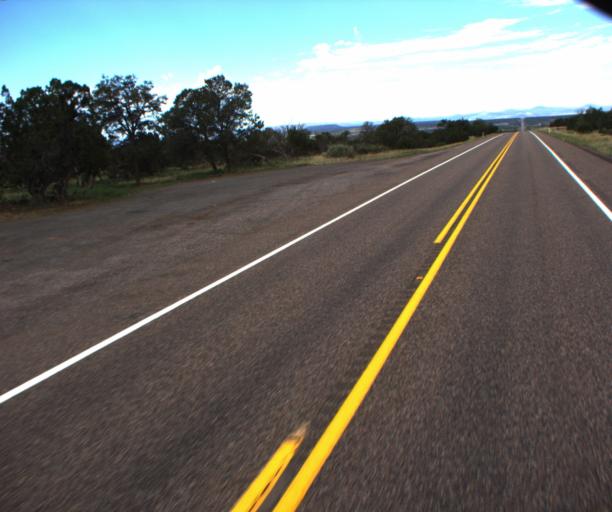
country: US
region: Arizona
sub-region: Apache County
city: Springerville
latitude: 34.1598
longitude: -109.0945
